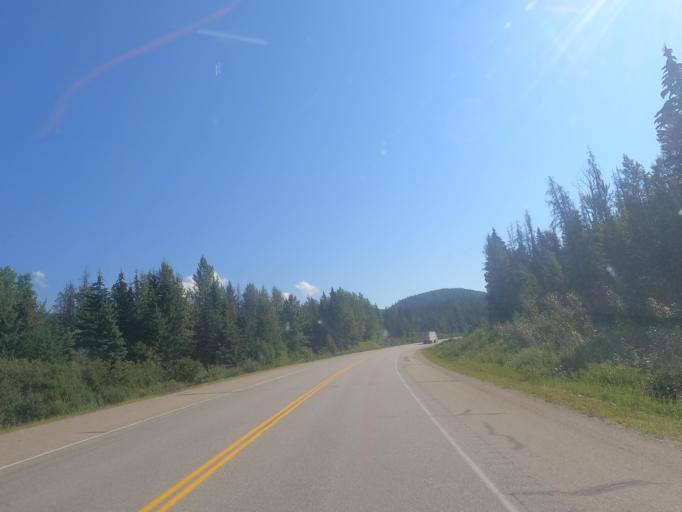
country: CA
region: Alberta
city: Jasper Park Lodge
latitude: 52.8880
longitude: -118.4774
